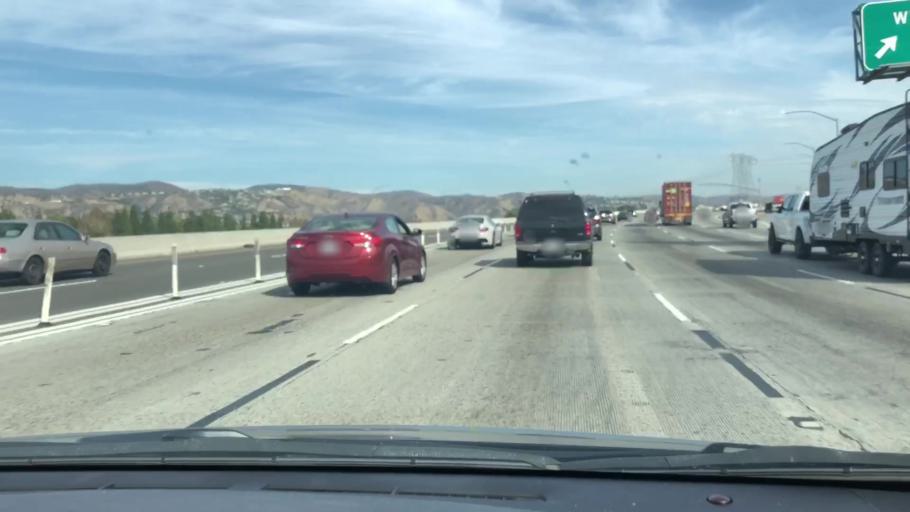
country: US
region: California
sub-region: Orange County
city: Yorba Linda
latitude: 33.8679
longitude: -117.7613
